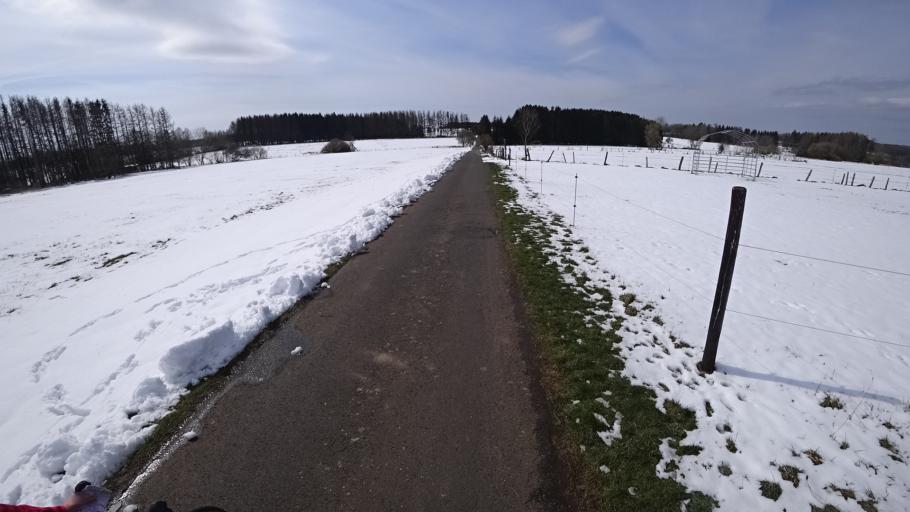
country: DE
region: Rheinland-Pfalz
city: Elkenroth
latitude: 50.7231
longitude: 7.8771
